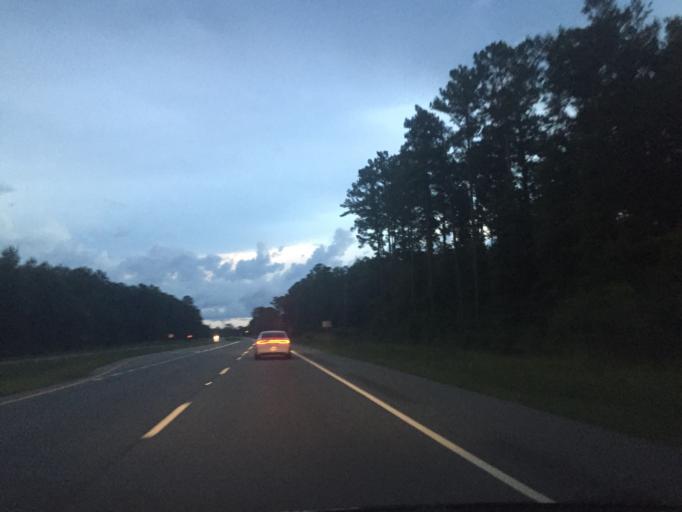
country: US
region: Georgia
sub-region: Liberty County
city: Midway
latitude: 31.8268
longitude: -81.5034
